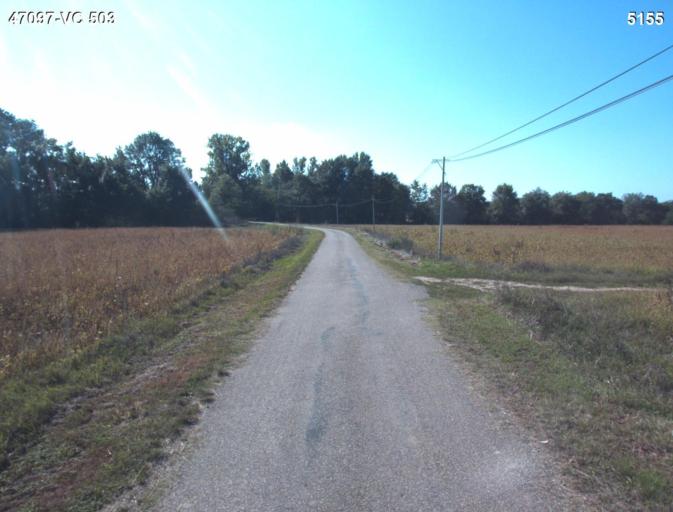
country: FR
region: Aquitaine
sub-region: Departement du Lot-et-Garonne
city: Port-Sainte-Marie
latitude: 44.2300
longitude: 0.3858
